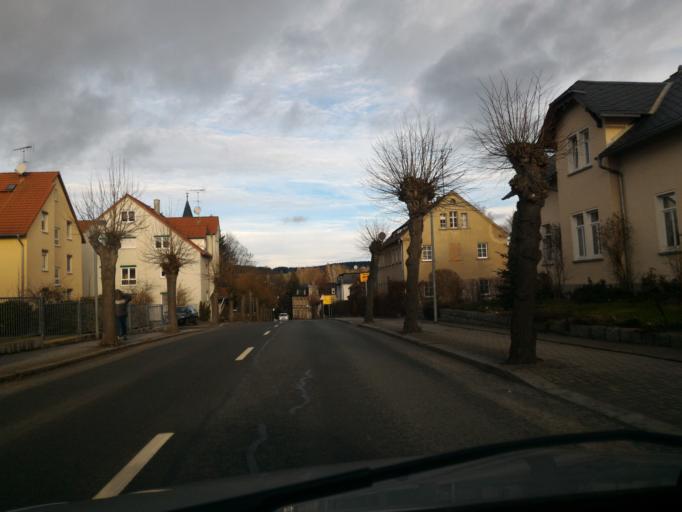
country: DE
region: Saxony
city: Oppach
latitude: 51.0569
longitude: 14.5043
